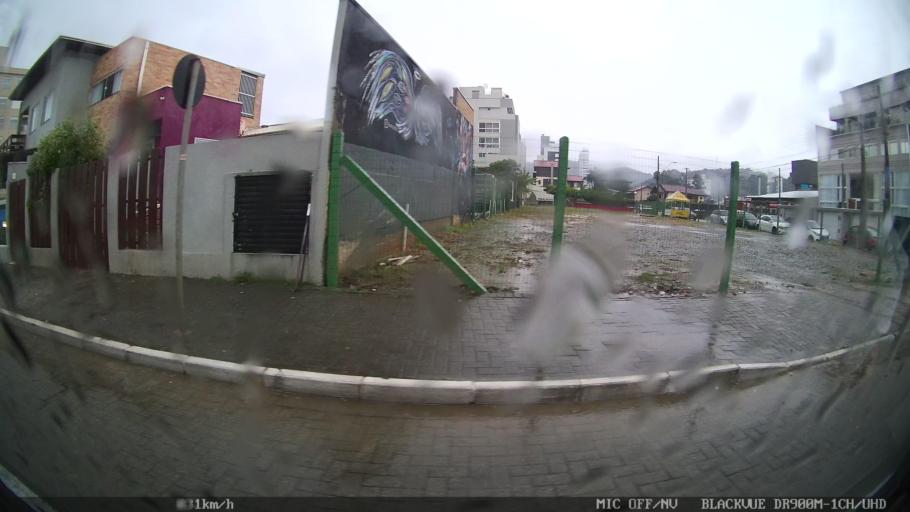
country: BR
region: Santa Catarina
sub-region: Balneario Camboriu
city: Balneario Camboriu
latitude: -26.9553
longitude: -48.6298
